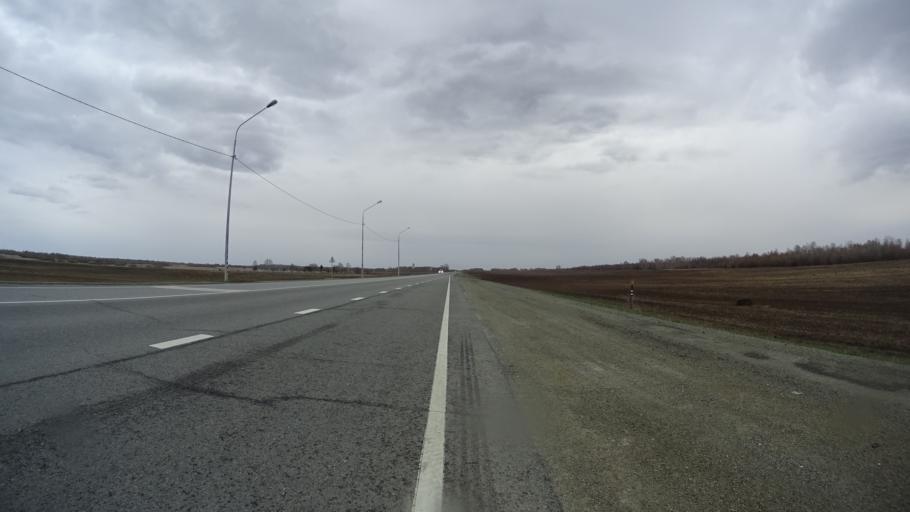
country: RU
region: Chelyabinsk
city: Krasnogorskiy
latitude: 54.6714
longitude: 61.2502
